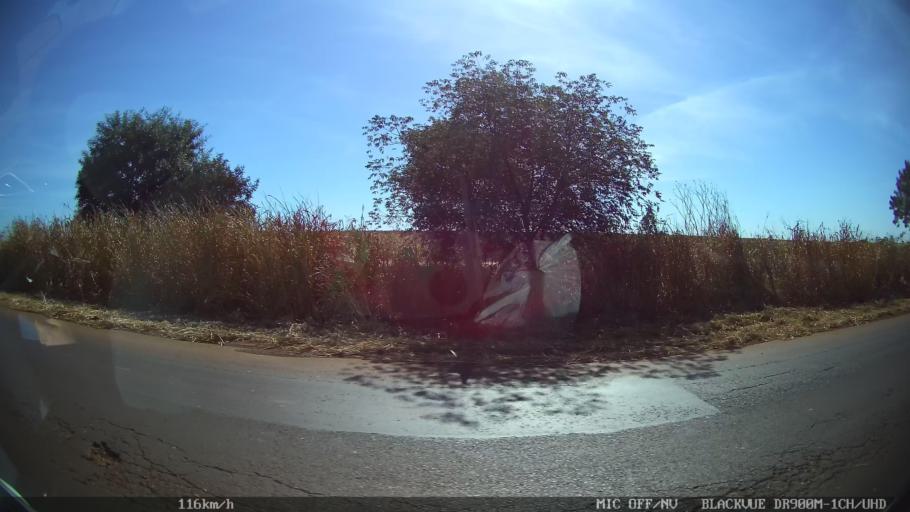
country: BR
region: Sao Paulo
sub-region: Barretos
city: Barretos
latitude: -20.4609
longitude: -48.4672
